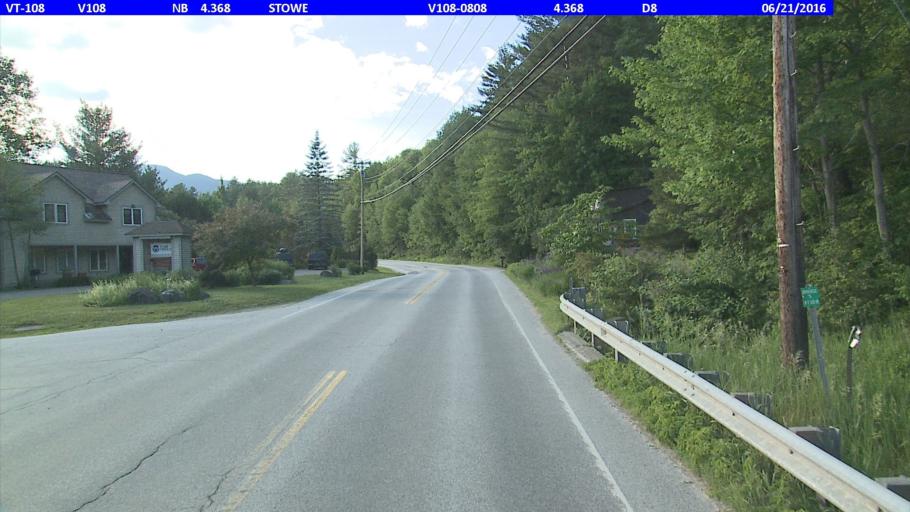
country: US
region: Vermont
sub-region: Lamoille County
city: Morristown
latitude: 44.4978
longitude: -72.7436
